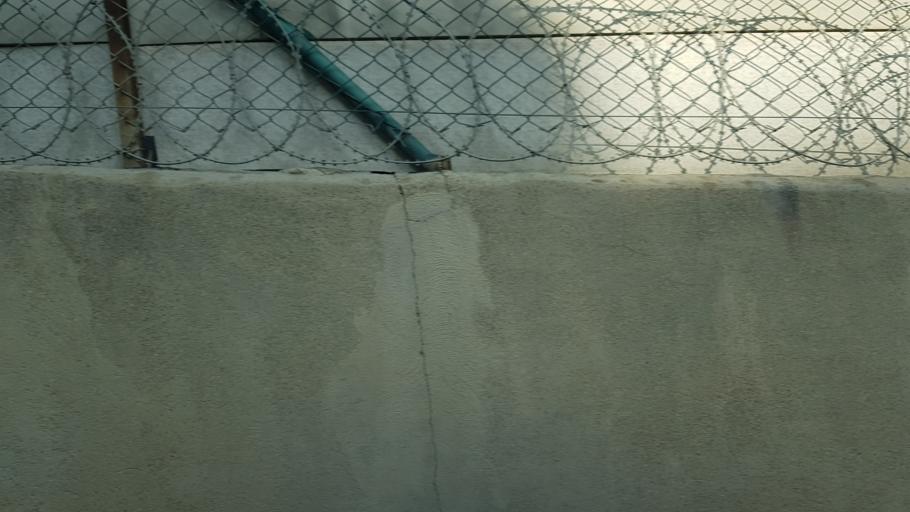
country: TR
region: Istanbul
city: Maltepe
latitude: 40.8998
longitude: 29.2015
